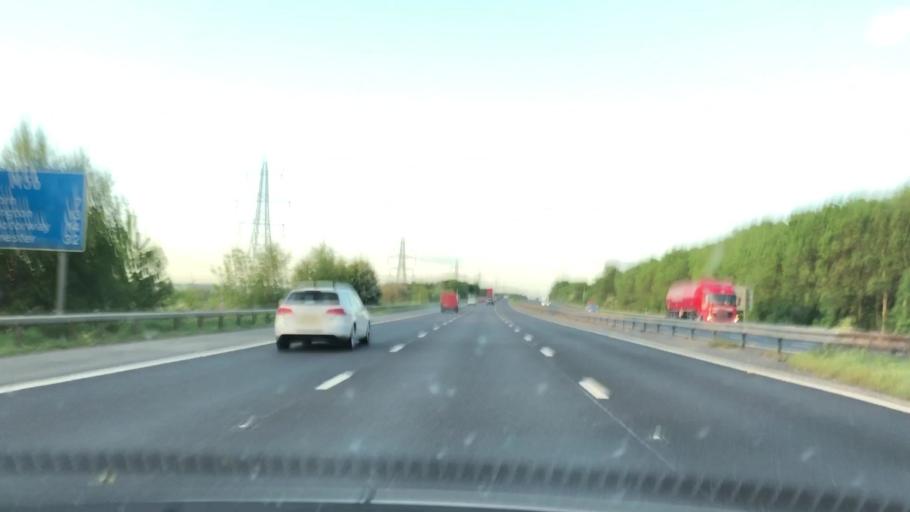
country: GB
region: England
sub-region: Cheshire West and Chester
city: Helsby
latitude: 53.2715
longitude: -2.7901
